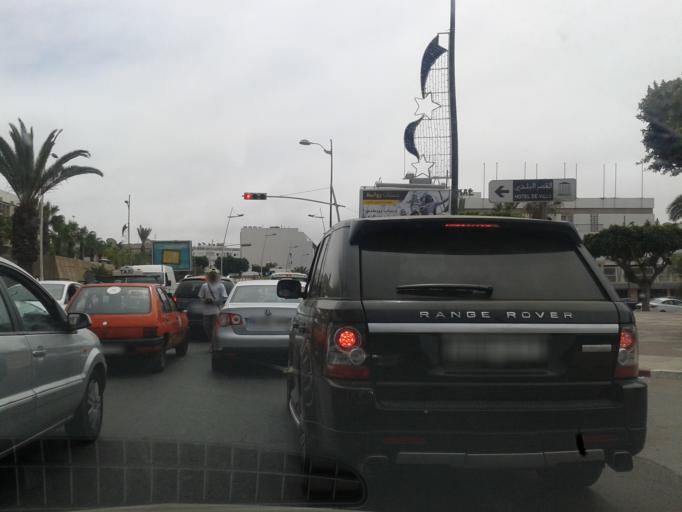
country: MA
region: Souss-Massa-Draa
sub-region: Agadir-Ida-ou-Tnan
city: Agadir
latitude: 30.4204
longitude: -9.5995
